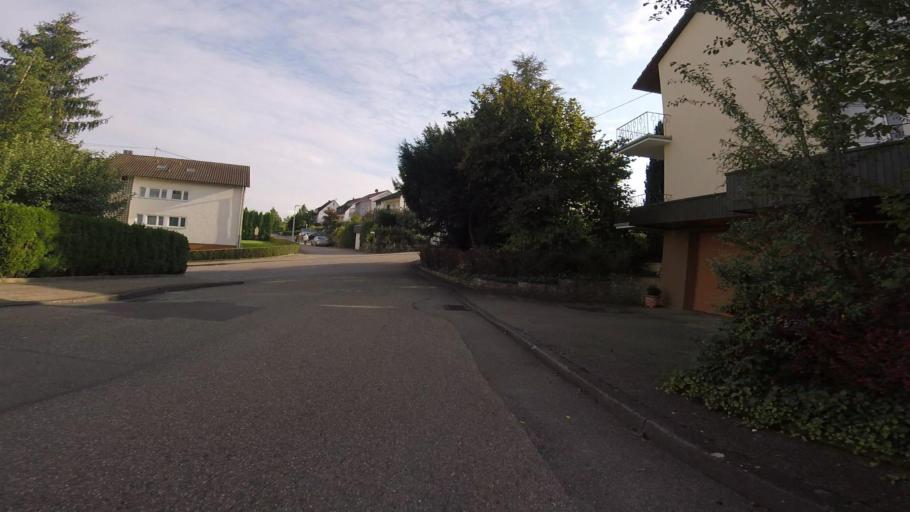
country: DE
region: Baden-Wuerttemberg
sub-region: Regierungsbezirk Stuttgart
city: Backnang
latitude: 48.9529
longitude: 9.4299
